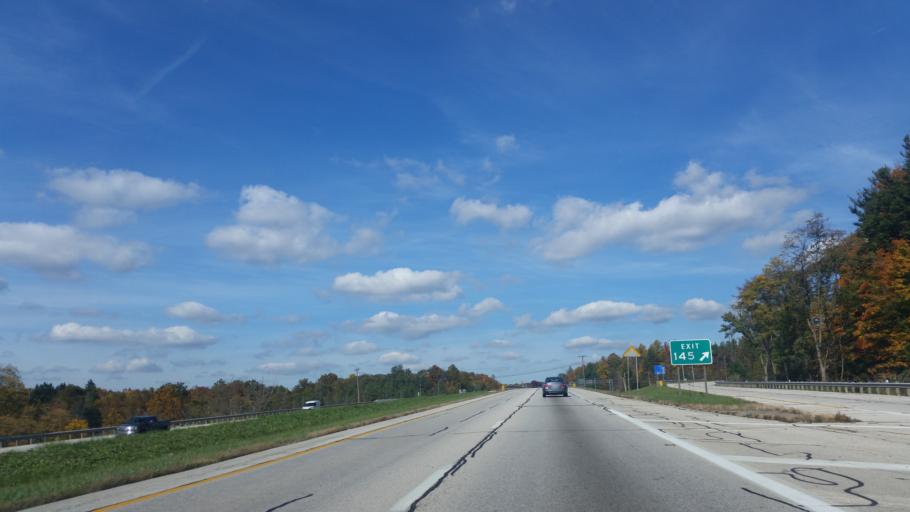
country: US
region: Ohio
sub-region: Summit County
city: Richfield
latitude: 41.2565
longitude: -81.6314
